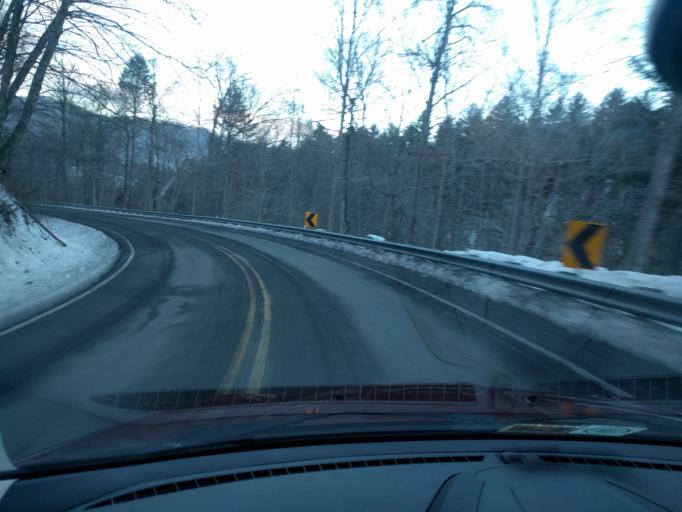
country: US
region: Virginia
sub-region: Bath County
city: Warm Springs
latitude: 38.0702
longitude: -79.8323
